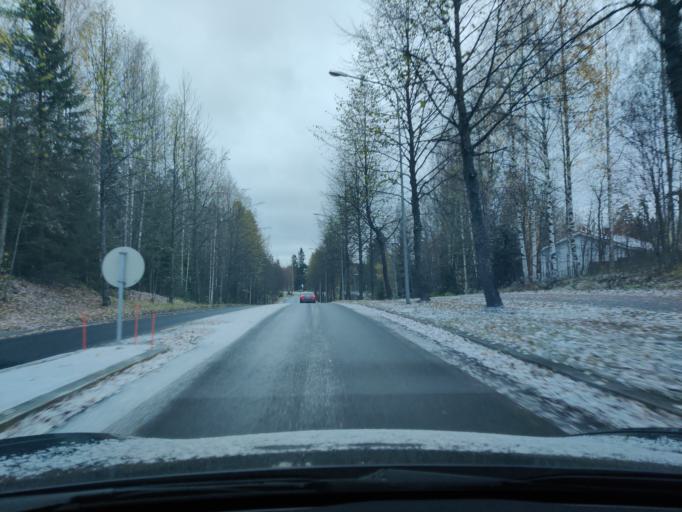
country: FI
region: Northern Savo
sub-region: Kuopio
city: Kuopio
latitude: 62.8399
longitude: 27.6352
